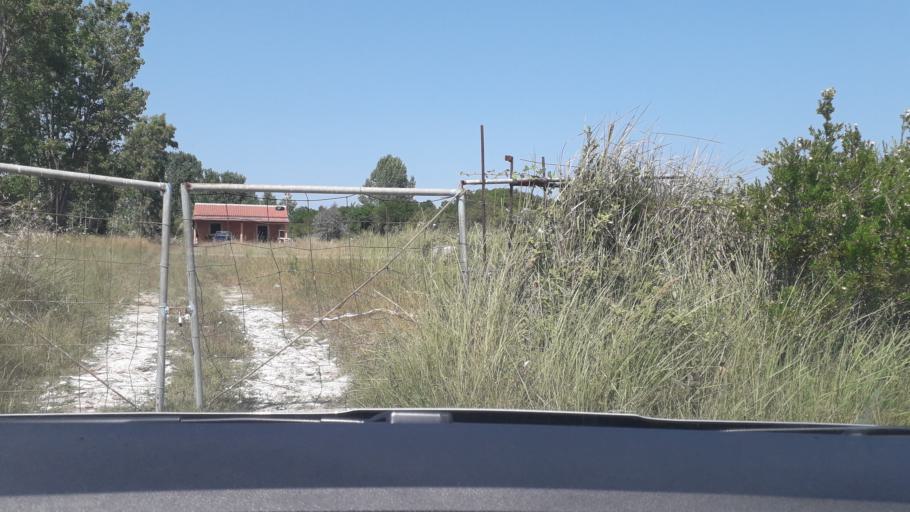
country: GR
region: Ionian Islands
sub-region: Nomos Kerkyras
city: Agios Matthaios
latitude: 39.4551
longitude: 19.8852
